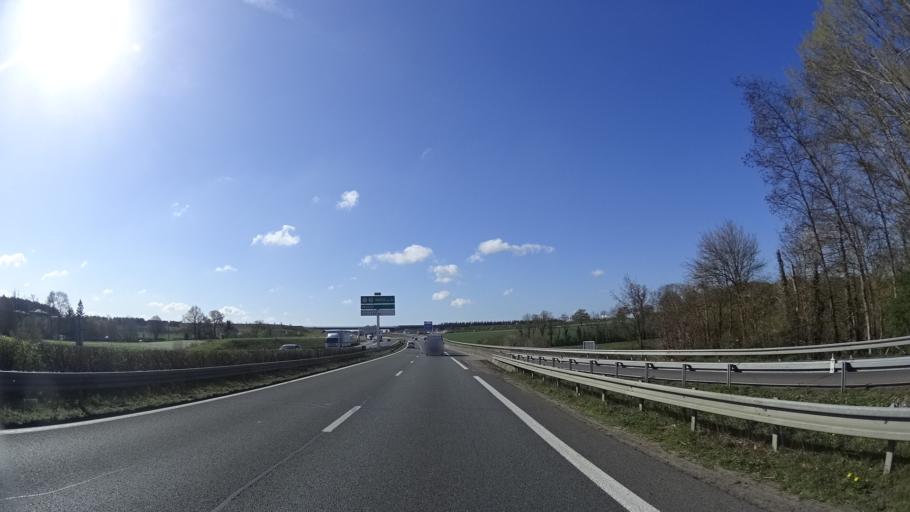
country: FR
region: Pays de la Loire
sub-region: Departement de Maine-et-Loire
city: Beaucouze
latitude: 47.4994
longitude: -0.6220
